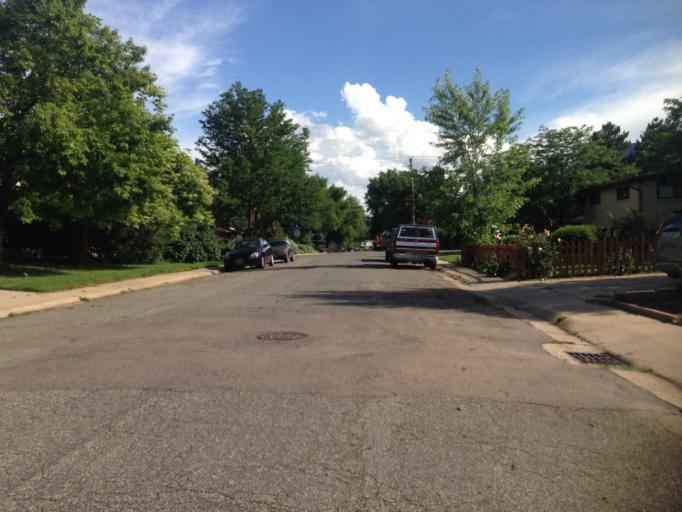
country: US
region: Colorado
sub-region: Boulder County
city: Boulder
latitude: 40.0286
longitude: -105.2749
